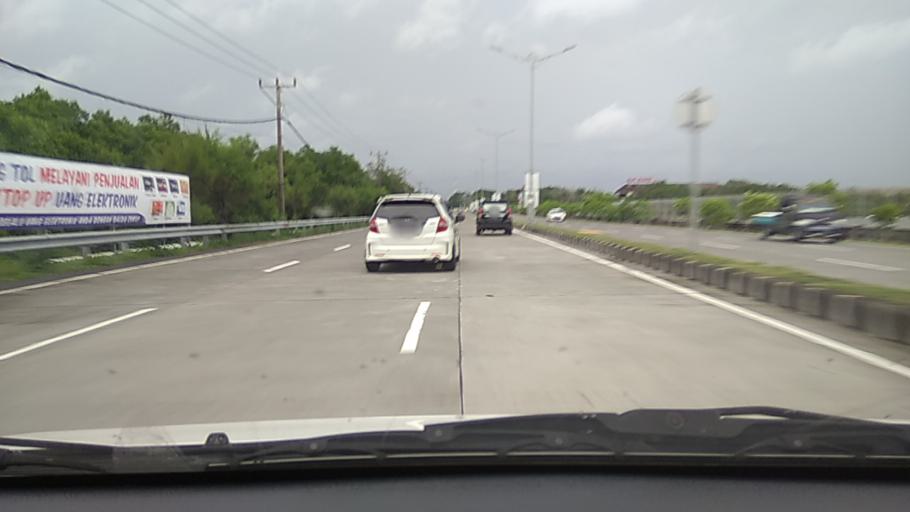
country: ID
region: Bali
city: Karyadharma
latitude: -8.7282
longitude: 115.2131
